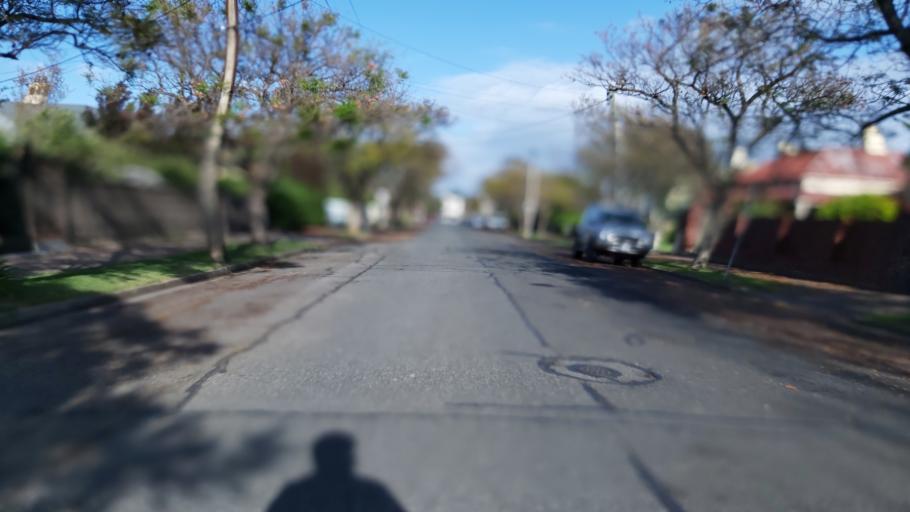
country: AU
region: South Australia
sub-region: Unley
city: Unley
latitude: -34.9482
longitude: 138.6109
